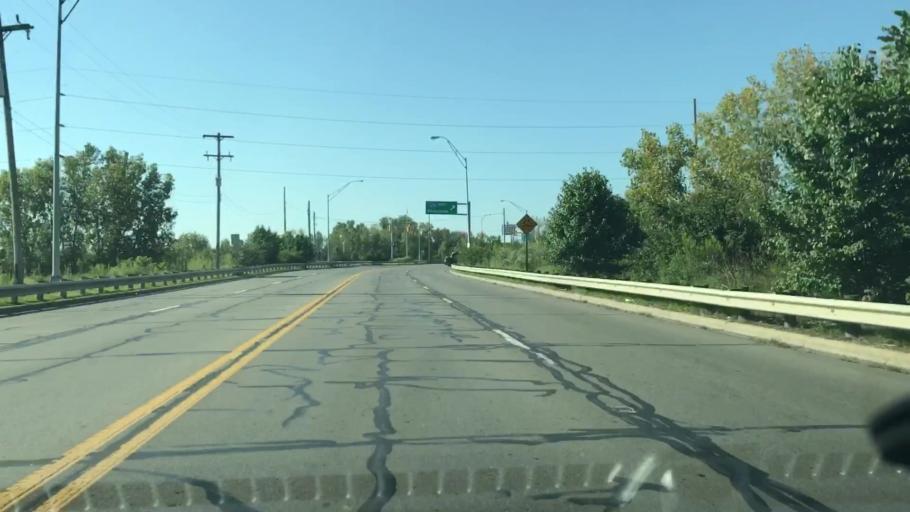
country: US
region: Ohio
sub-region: Franklin County
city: Bexley
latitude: 39.9825
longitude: -82.9561
